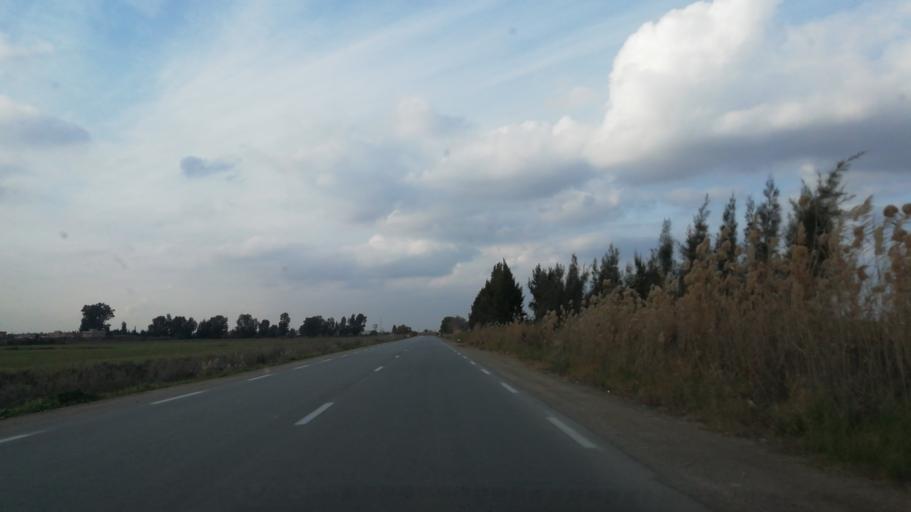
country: DZ
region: Mascara
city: Sig
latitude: 35.6460
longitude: 0.0268
